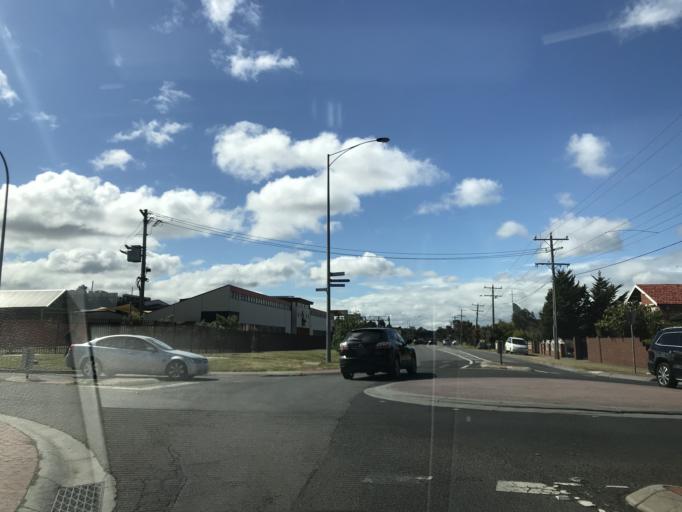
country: AU
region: Victoria
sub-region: Brimbank
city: Deer Park
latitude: -37.7865
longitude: 144.7910
